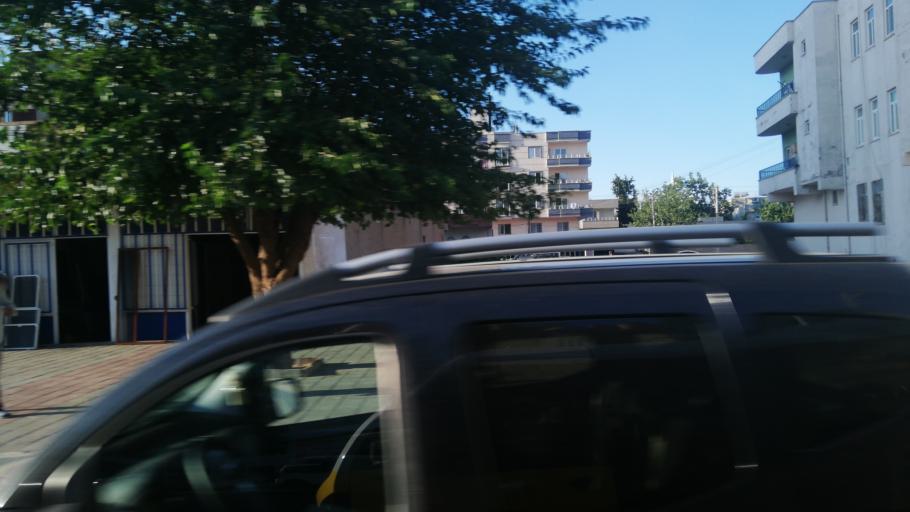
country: TR
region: Mardin
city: Midyat
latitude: 37.4167
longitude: 41.3655
